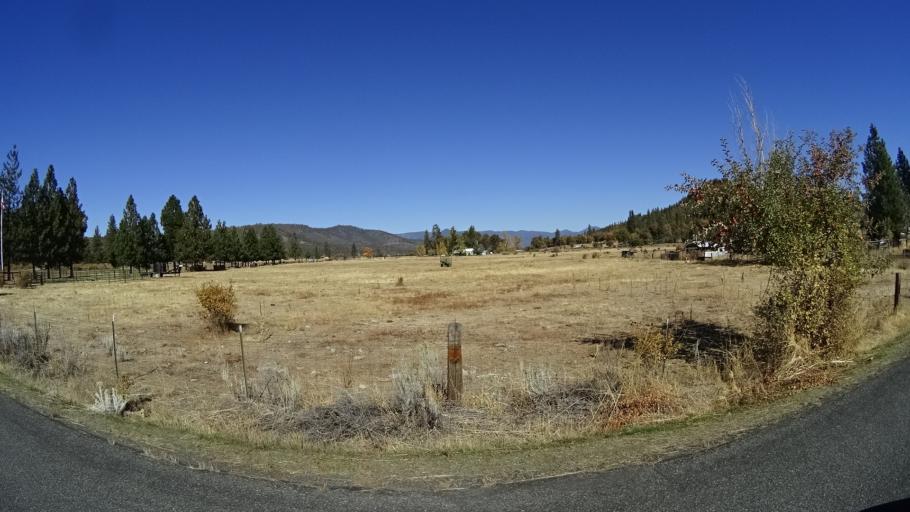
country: US
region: California
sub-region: Siskiyou County
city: Yreka
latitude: 41.5485
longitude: -122.9185
